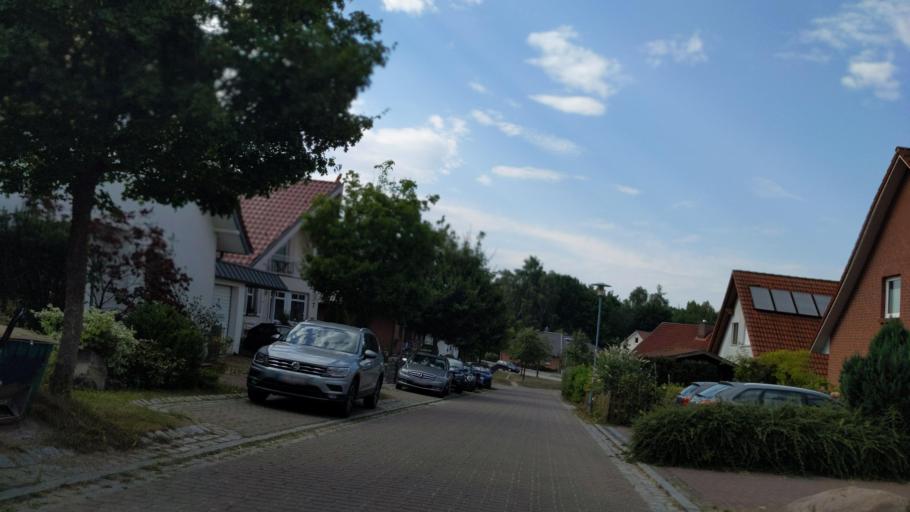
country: DE
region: Schleswig-Holstein
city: Gross Gronau
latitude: 53.8424
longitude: 10.7673
